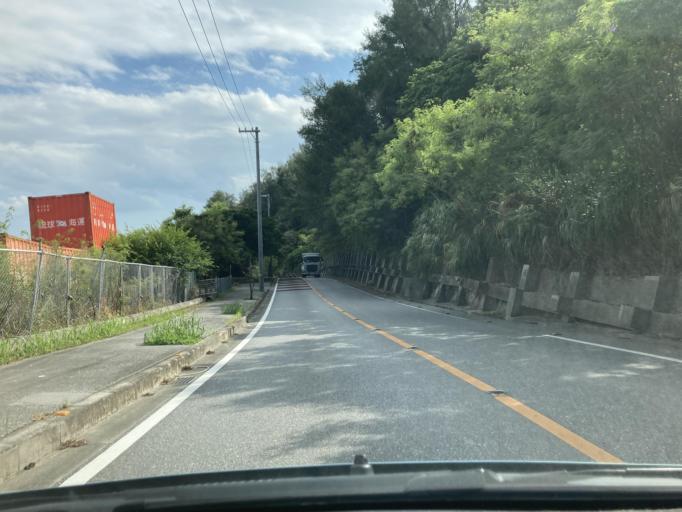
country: JP
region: Okinawa
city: Ginowan
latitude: 26.2626
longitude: 127.7836
